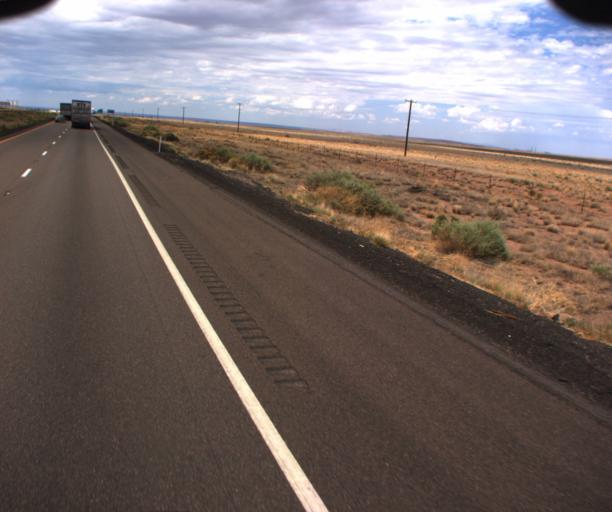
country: US
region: Arizona
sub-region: Navajo County
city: Holbrook
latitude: 34.9572
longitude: -110.1099
